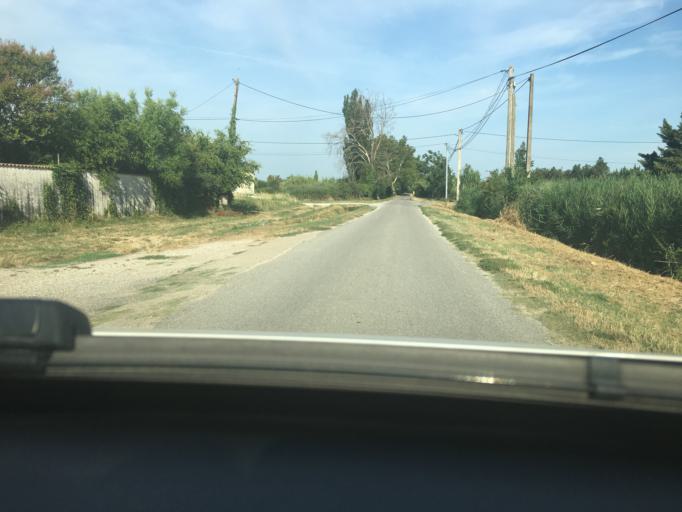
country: FR
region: Provence-Alpes-Cote d'Azur
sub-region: Departement des Bouches-du-Rhone
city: Eyragues
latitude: 43.8323
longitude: 4.8220
